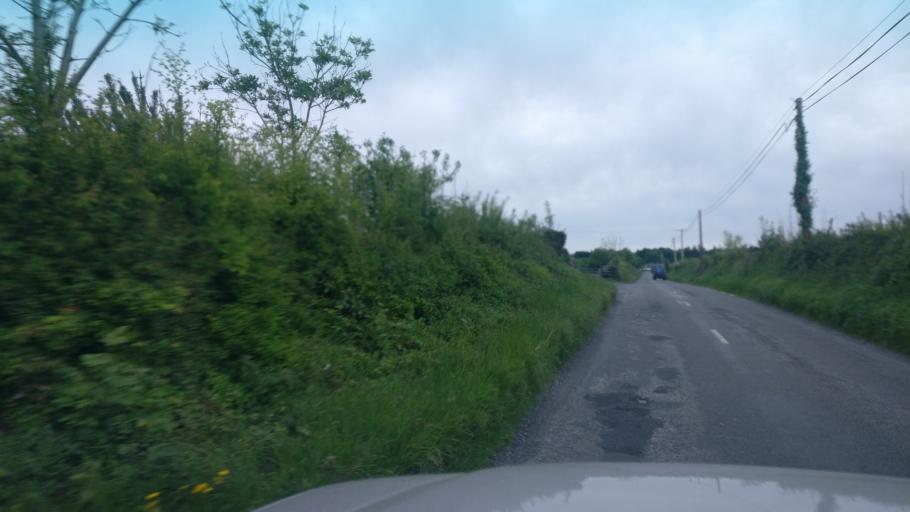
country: IE
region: Connaught
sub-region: County Galway
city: Portumna
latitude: 53.0946
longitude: -8.2397
